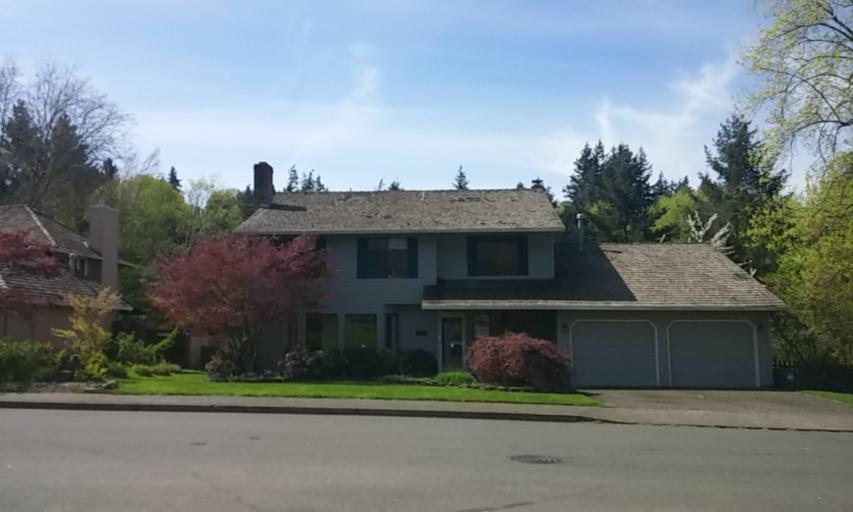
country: US
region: Oregon
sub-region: Washington County
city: West Haven-Sylvan
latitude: 45.5175
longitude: -122.7492
